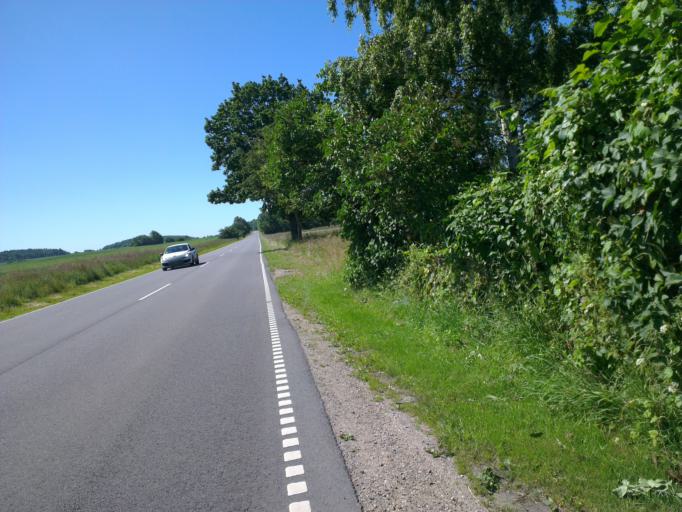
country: DK
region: Capital Region
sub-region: Frederikssund Kommune
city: Jaegerspris
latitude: 55.8860
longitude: 11.9552
